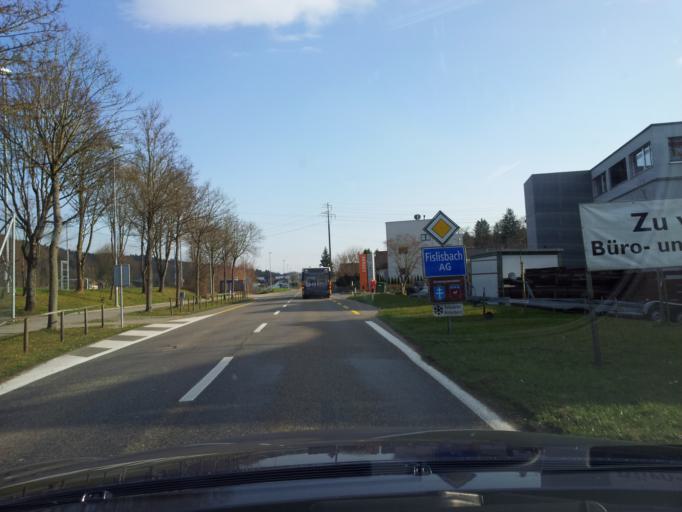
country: CH
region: Aargau
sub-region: Bezirk Baden
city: Niederrohrdorf
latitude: 47.4445
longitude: 8.2943
